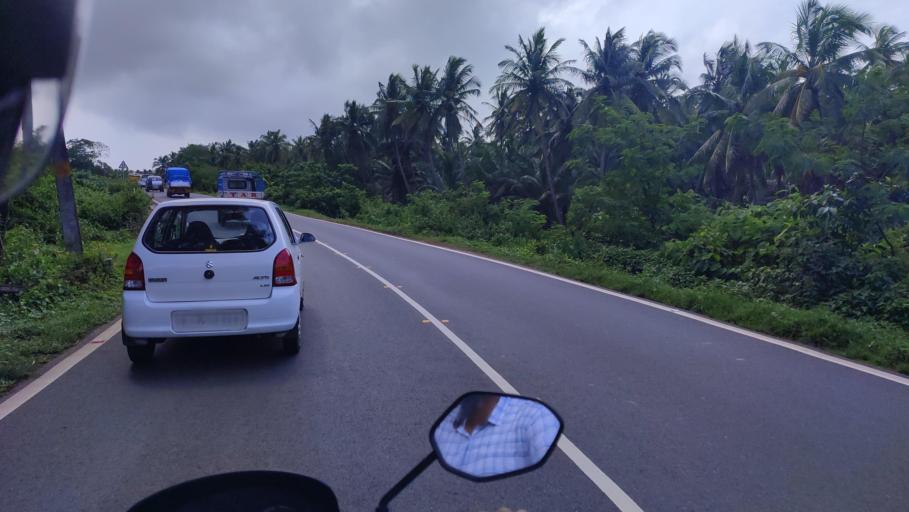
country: IN
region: Kerala
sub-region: Kasaragod District
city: Nileshwar
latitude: 12.2337
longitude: 75.1541
